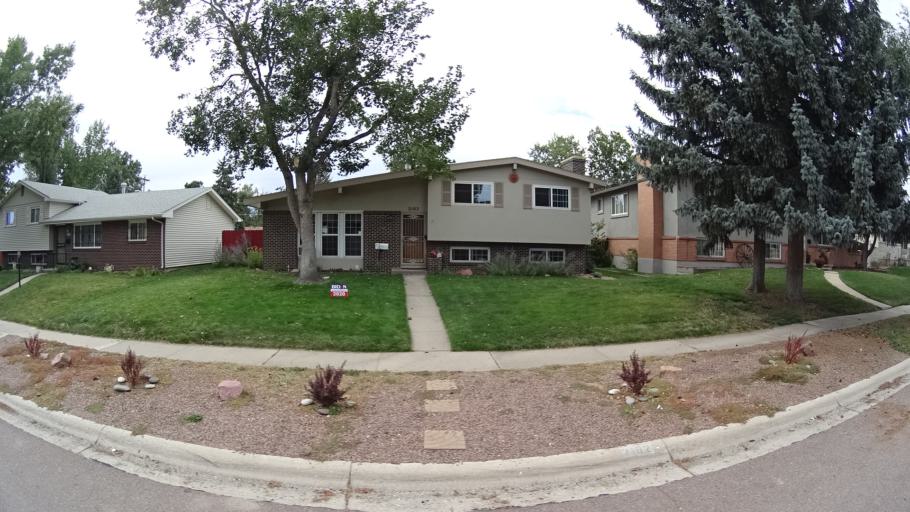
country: US
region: Colorado
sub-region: El Paso County
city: Colorado Springs
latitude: 38.8611
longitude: -104.7839
